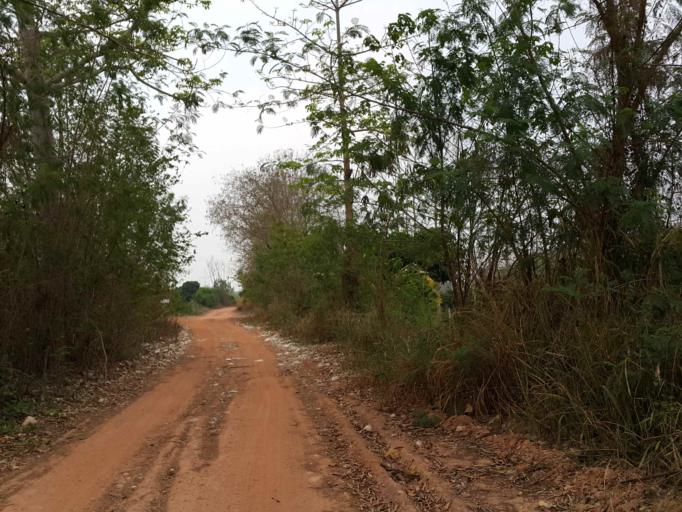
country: TH
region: Chiang Mai
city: Mae Taeng
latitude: 19.1161
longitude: 98.9969
